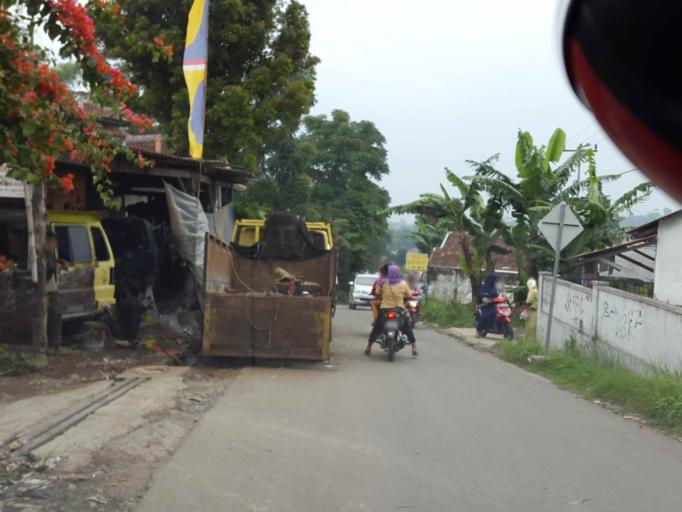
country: ID
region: West Java
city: Lembang
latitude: -6.8095
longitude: 107.5875
